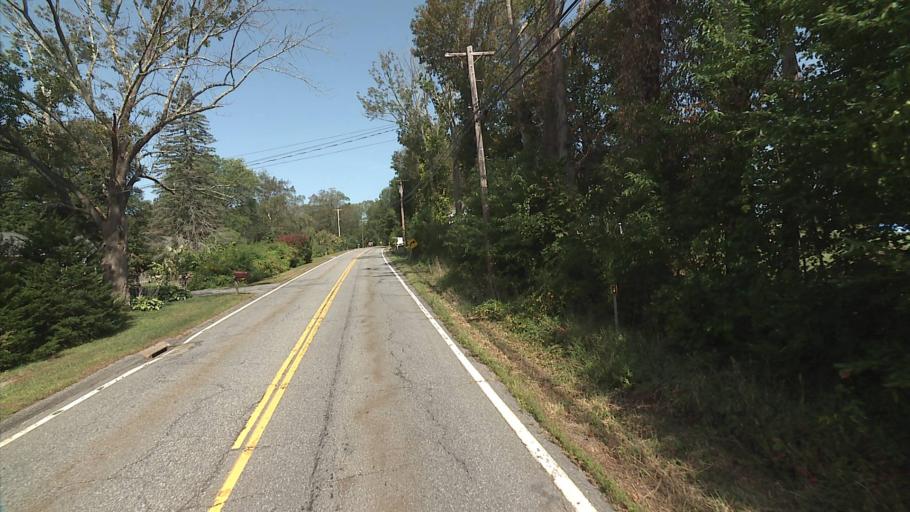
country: US
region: Connecticut
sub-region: Windham County
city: South Woodstock
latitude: 41.9697
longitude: -71.9887
